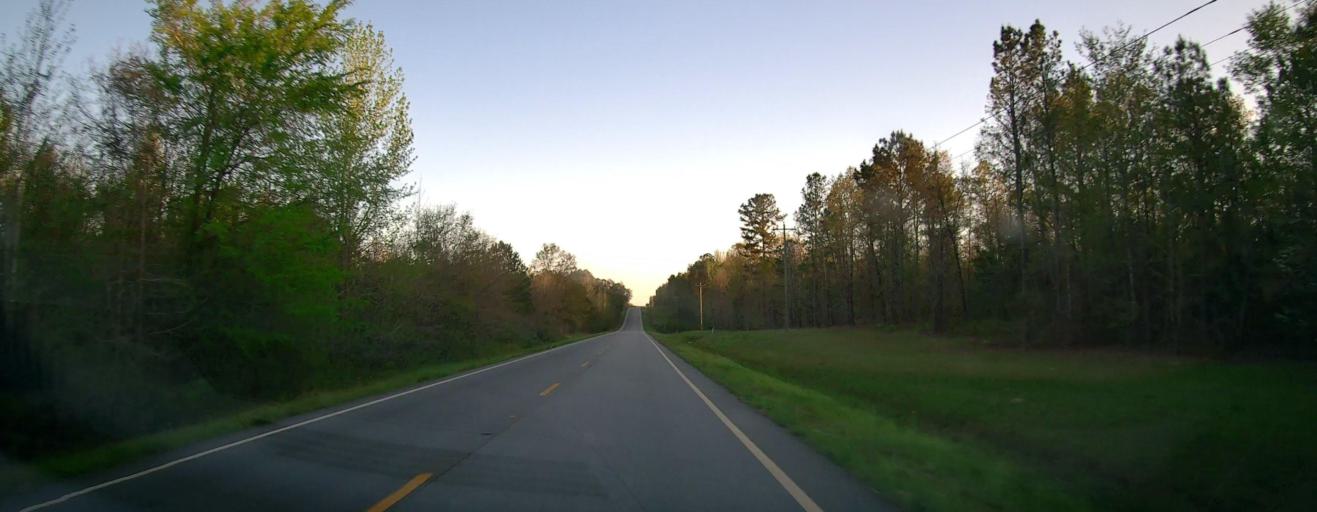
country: US
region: Georgia
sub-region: Talbot County
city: Talbotton
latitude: 32.5515
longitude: -84.5696
